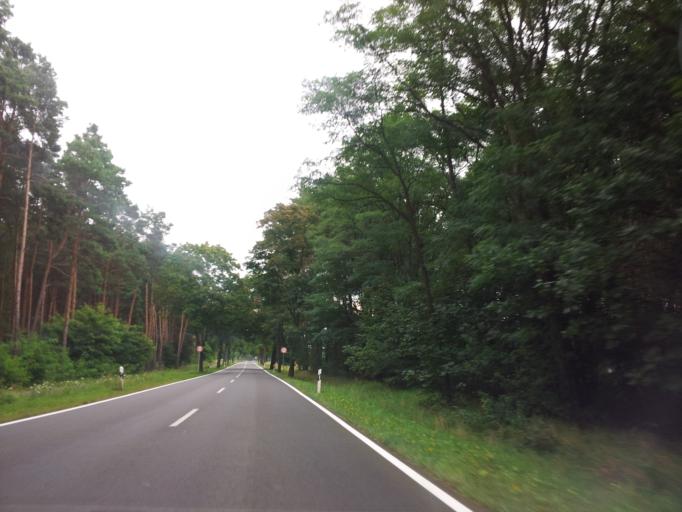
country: DE
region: Brandenburg
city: Linthe
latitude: 52.0951
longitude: 12.7865
